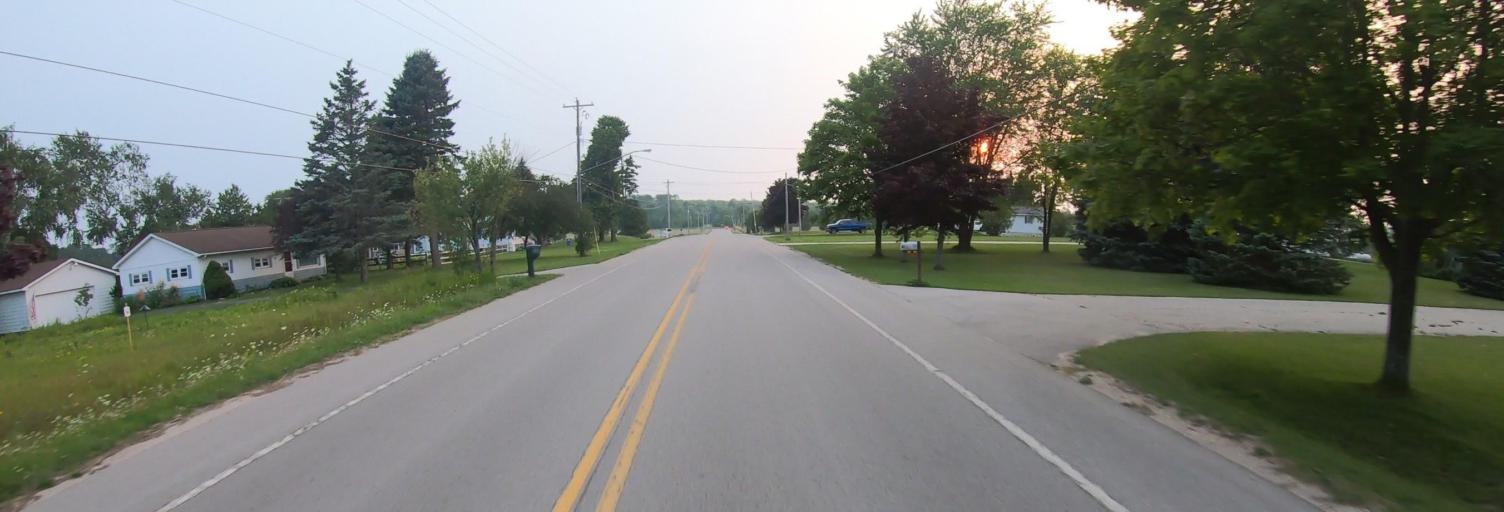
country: US
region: Michigan
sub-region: Mackinac County
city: Saint Ignace
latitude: 45.7817
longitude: -84.7666
